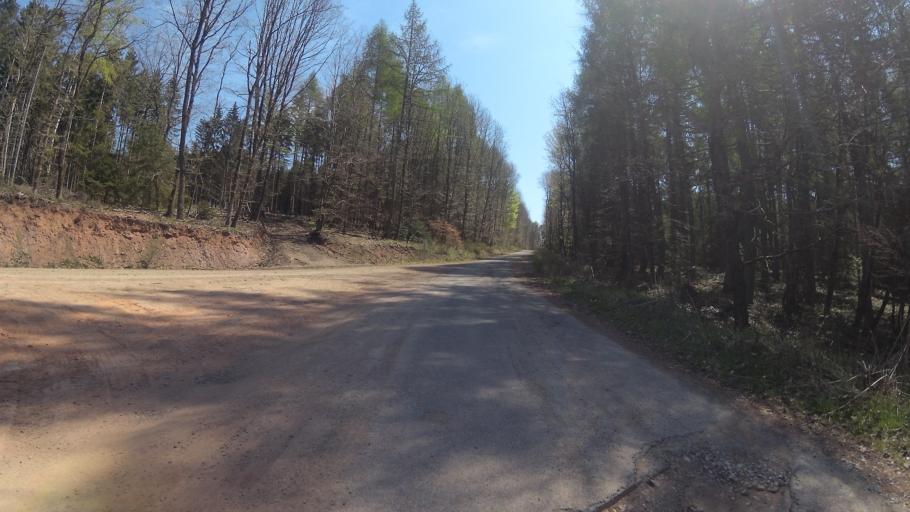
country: DE
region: Rheinland-Pfalz
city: Dunzweiler
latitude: 49.4078
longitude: 7.2878
